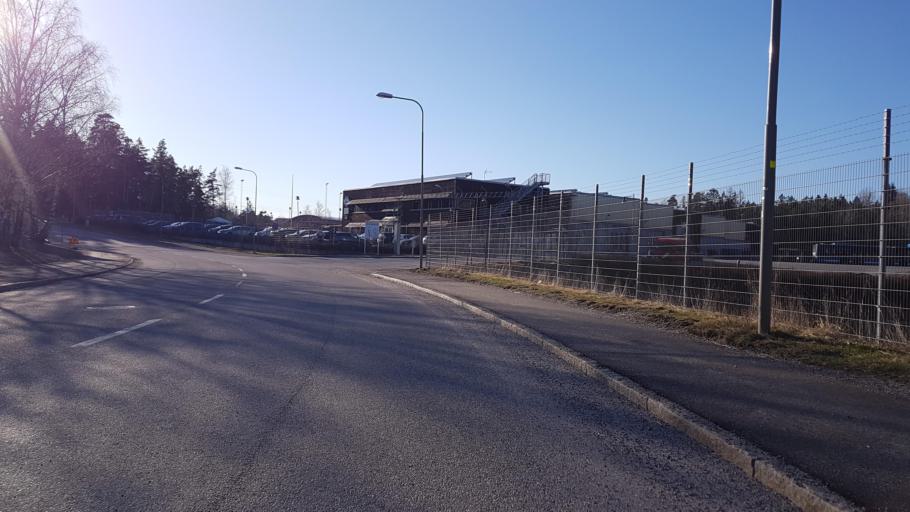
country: SE
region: Stockholm
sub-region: Stockholms Kommun
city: Arsta
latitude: 59.2635
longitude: 18.0685
